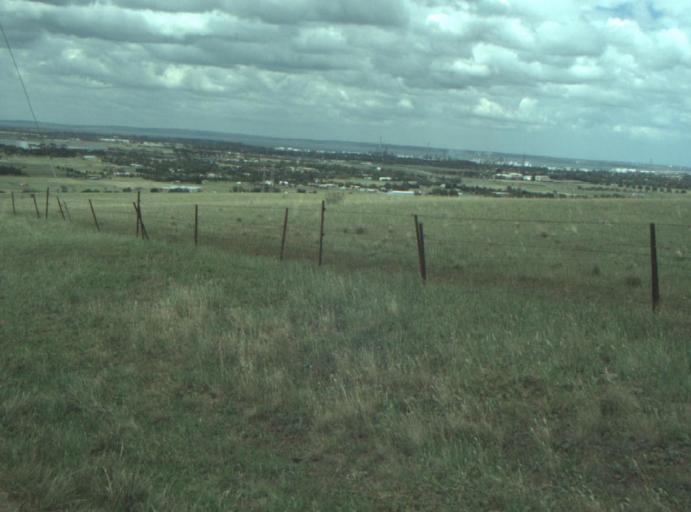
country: AU
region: Victoria
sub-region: Greater Geelong
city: Bell Post Hill
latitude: -38.0456
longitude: 144.3380
